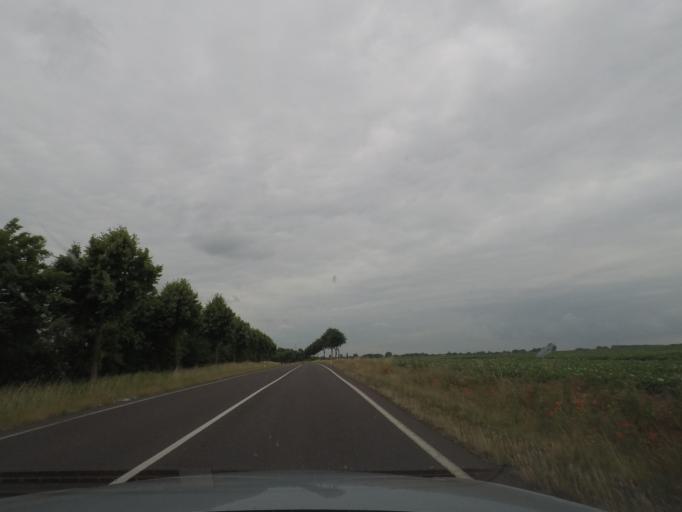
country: DE
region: Saxony-Anhalt
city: Erxleben
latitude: 52.2070
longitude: 11.2813
